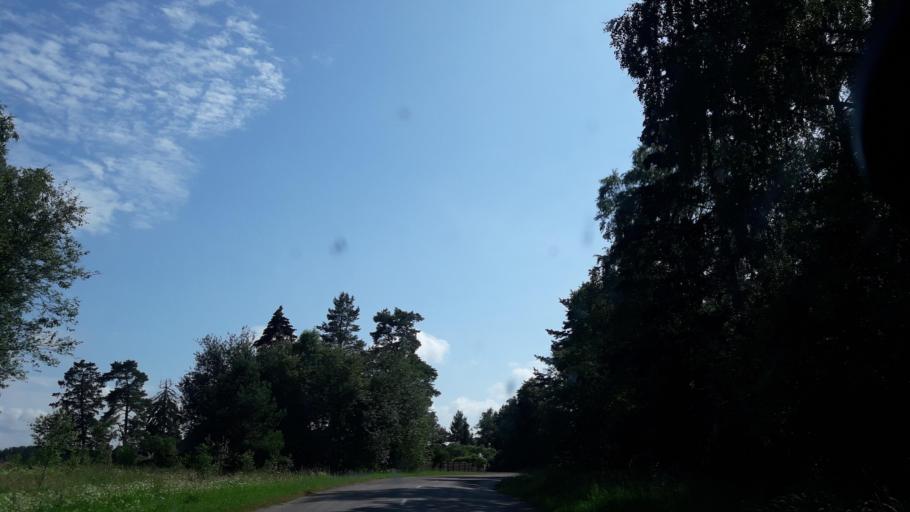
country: LV
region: Ventspils
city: Ventspils
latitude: 57.5046
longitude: 21.8474
